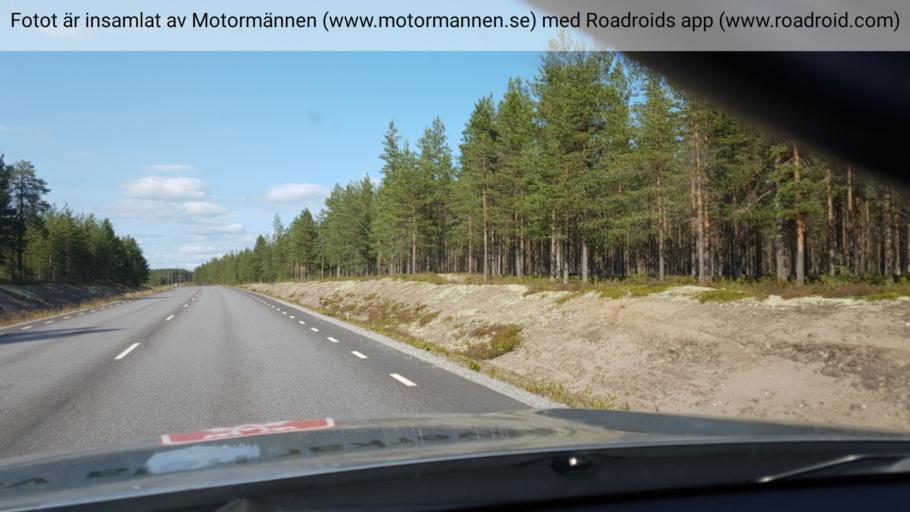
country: SE
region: Norrbotten
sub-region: Pitea Kommun
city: Pitea
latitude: 65.2560
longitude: 21.5383
